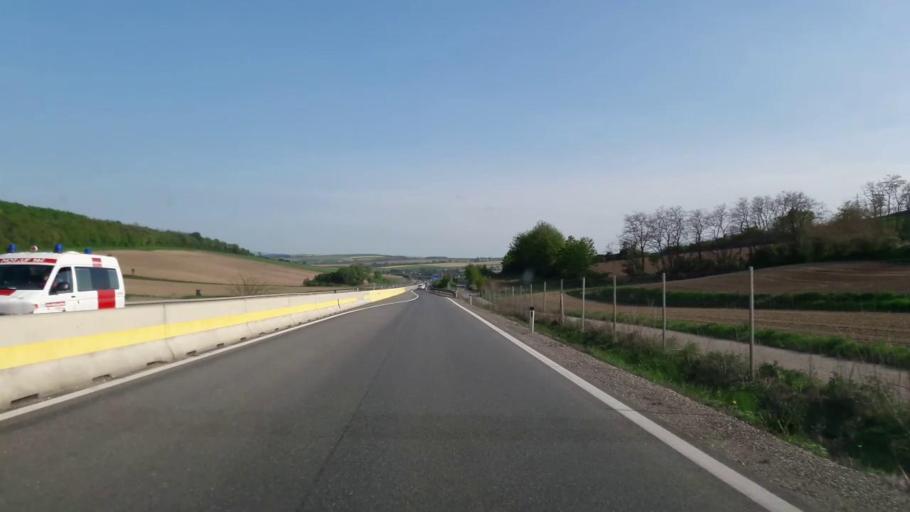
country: AT
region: Lower Austria
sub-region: Politischer Bezirk Hollabrunn
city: Hollabrunn
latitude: 48.5231
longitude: 16.0840
